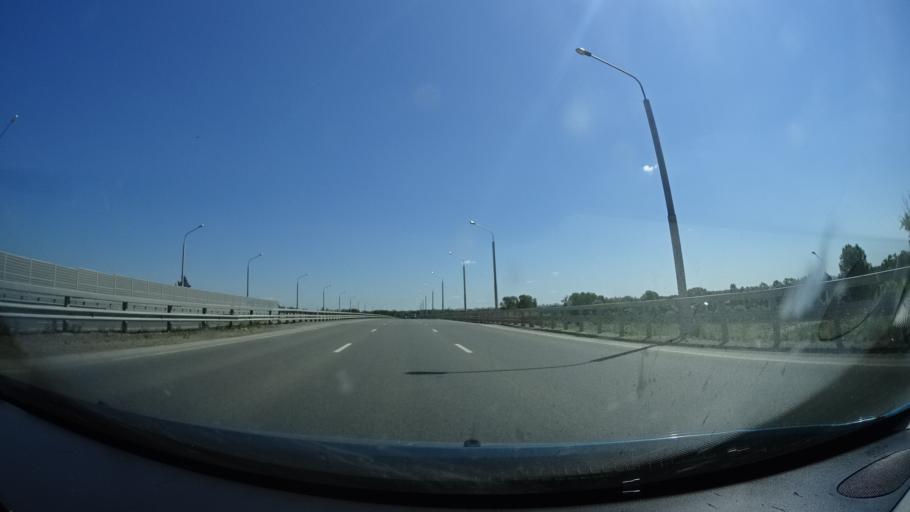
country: RU
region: Bashkortostan
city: Mikhaylovka
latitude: 54.7974
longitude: 55.8896
